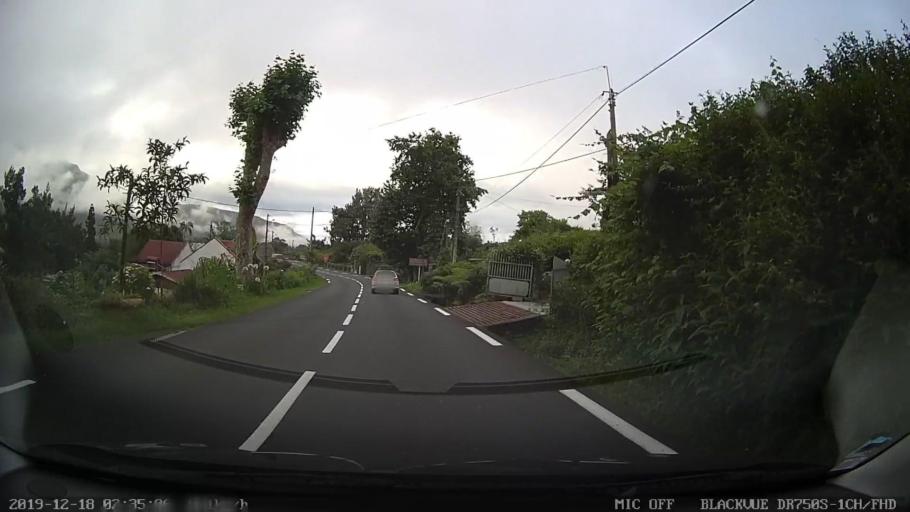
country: RE
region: Reunion
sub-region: Reunion
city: Salazie
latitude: -21.1491
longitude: 55.6152
